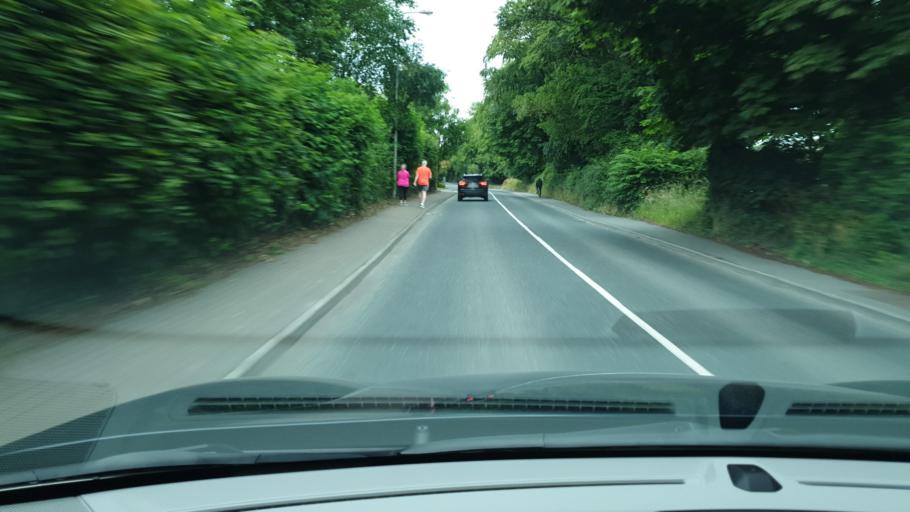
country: IE
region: Leinster
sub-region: An Mhi
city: Dunboyne
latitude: 53.4233
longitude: -6.4832
